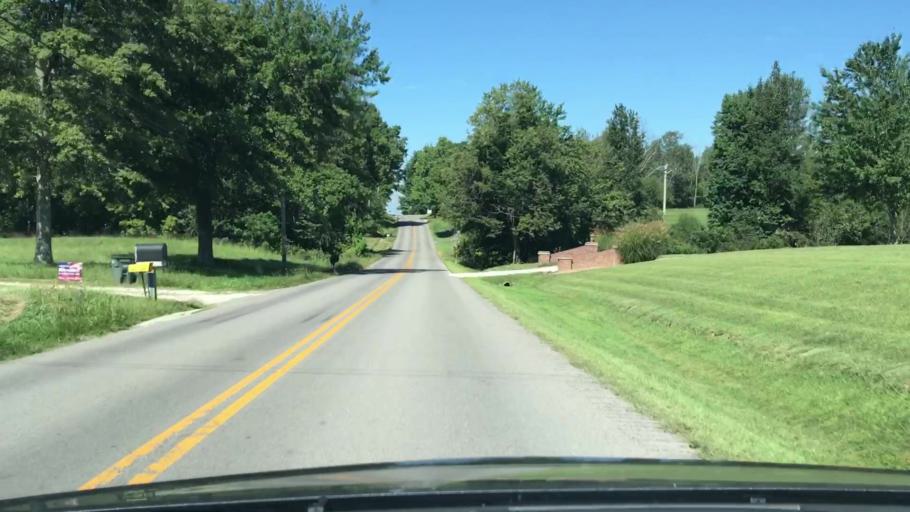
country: US
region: Kentucky
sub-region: Hardin County
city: Elizabethtown
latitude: 37.6007
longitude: -85.8819
